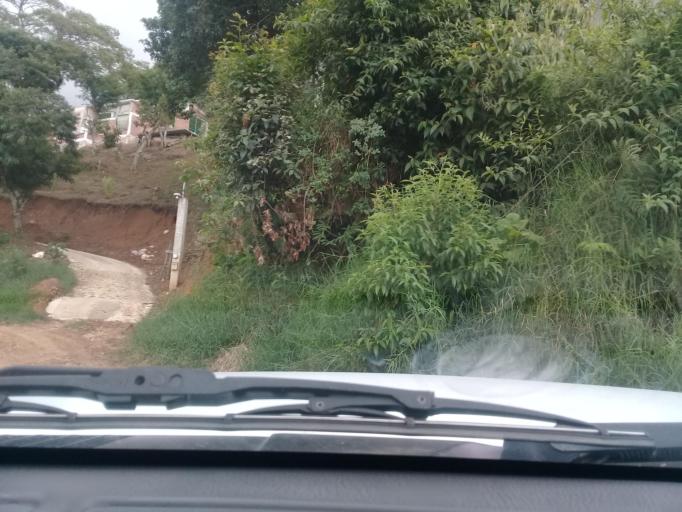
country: MX
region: Veracruz
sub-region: Tlalnelhuayocan
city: Guadalupe Victoria
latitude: 19.5564
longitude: -96.9576
